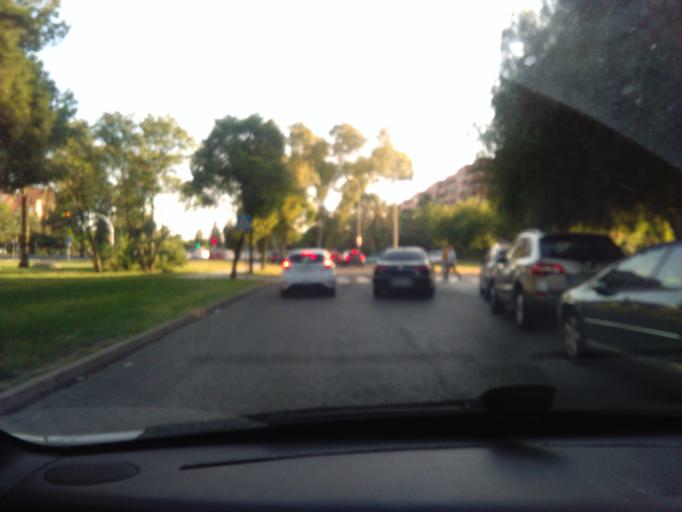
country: ES
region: Andalusia
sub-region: Provincia de Sevilla
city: Sevilla
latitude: 37.4030
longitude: -5.9422
